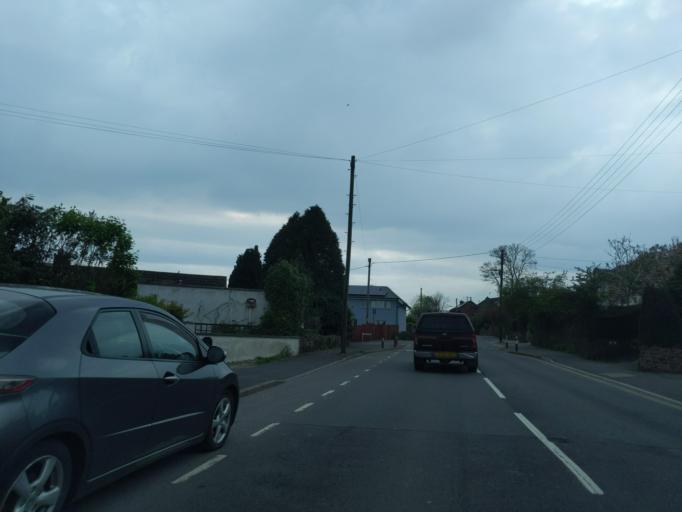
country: GB
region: England
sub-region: Devon
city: Crediton
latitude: 50.7922
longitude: -3.6702
